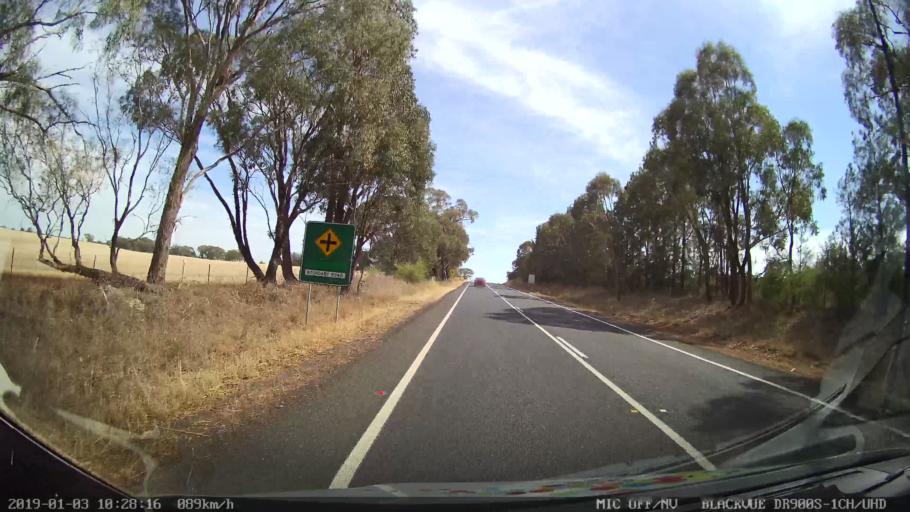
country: AU
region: New South Wales
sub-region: Young
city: Young
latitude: -34.3903
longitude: 148.2586
